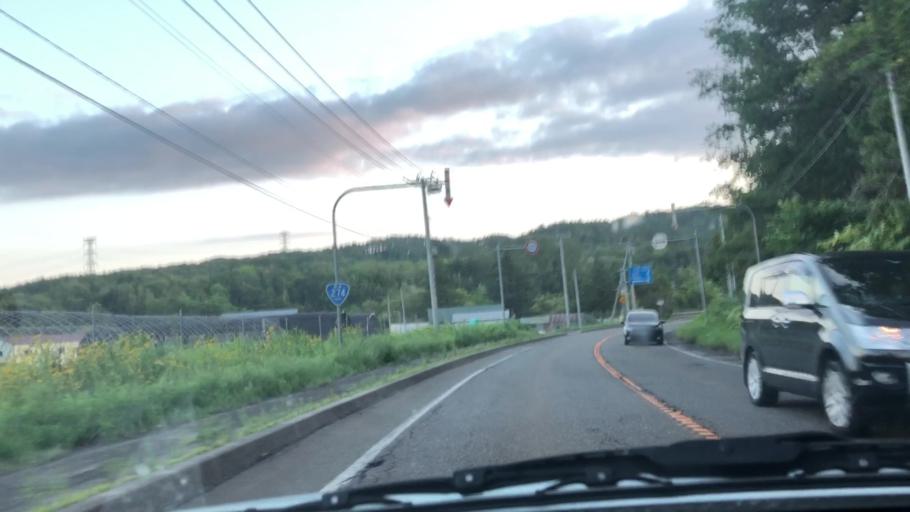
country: JP
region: Hokkaido
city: Chitose
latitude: 42.8706
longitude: 142.1628
